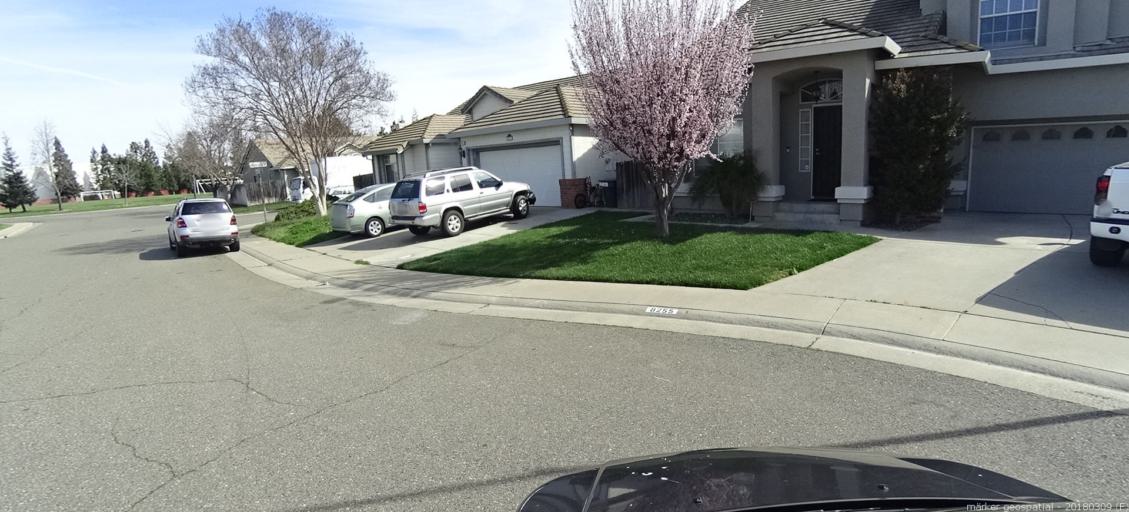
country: US
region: California
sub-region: Sacramento County
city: Florin
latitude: 38.4568
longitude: -121.4036
